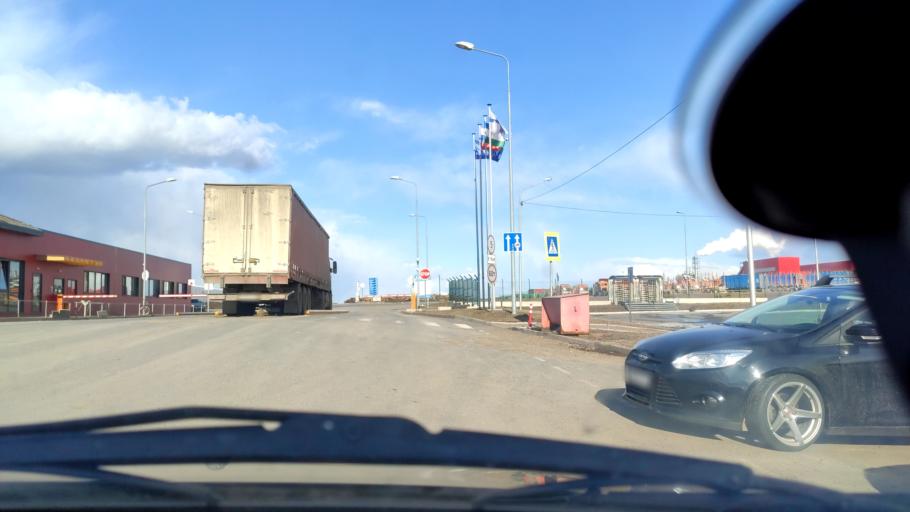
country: RU
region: Bashkortostan
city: Iglino
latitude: 54.7678
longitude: 56.2664
